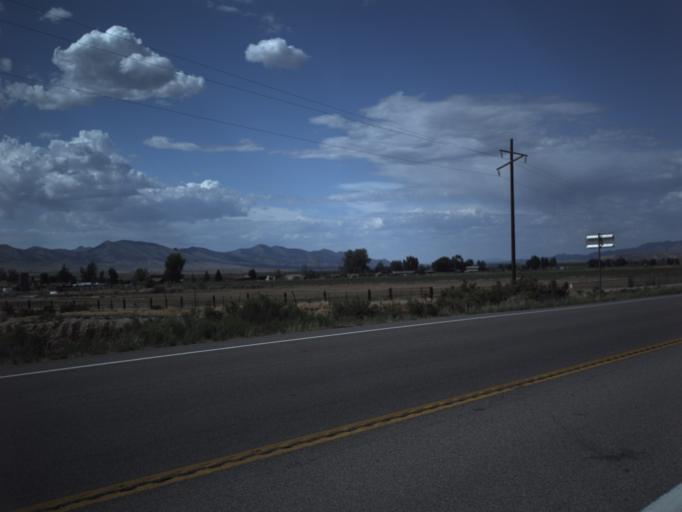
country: US
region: Utah
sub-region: Sanpete County
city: Centerfield
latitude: 39.0454
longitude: -111.8251
